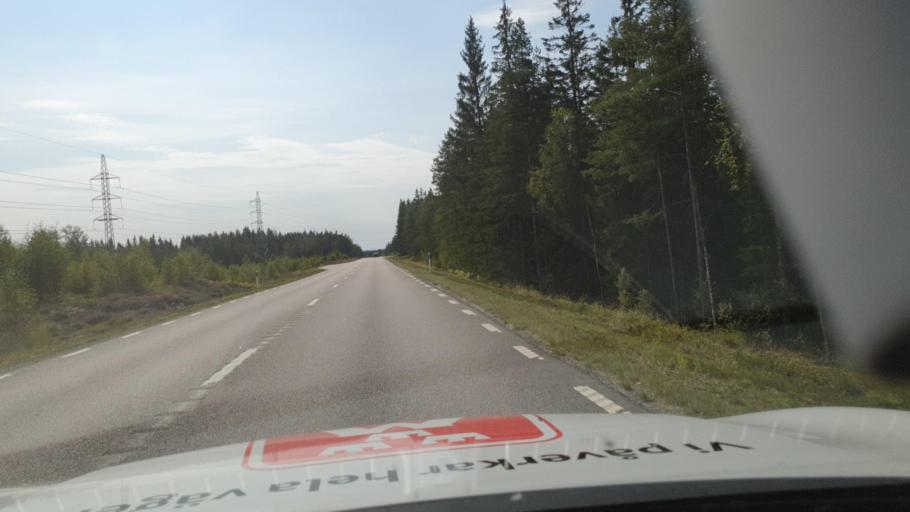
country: SE
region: Vaestra Goetaland
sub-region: Dals-Ed Kommun
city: Ed
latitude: 58.8625
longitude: 11.7732
